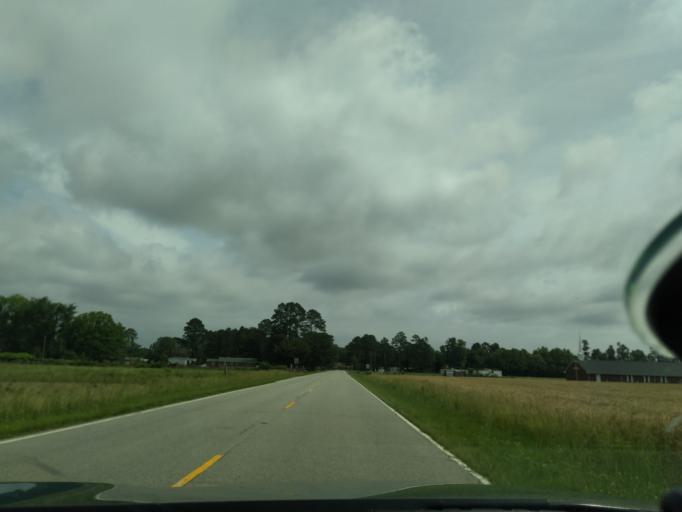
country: US
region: North Carolina
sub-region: Chowan County
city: Edenton
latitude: 35.9147
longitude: -76.6011
